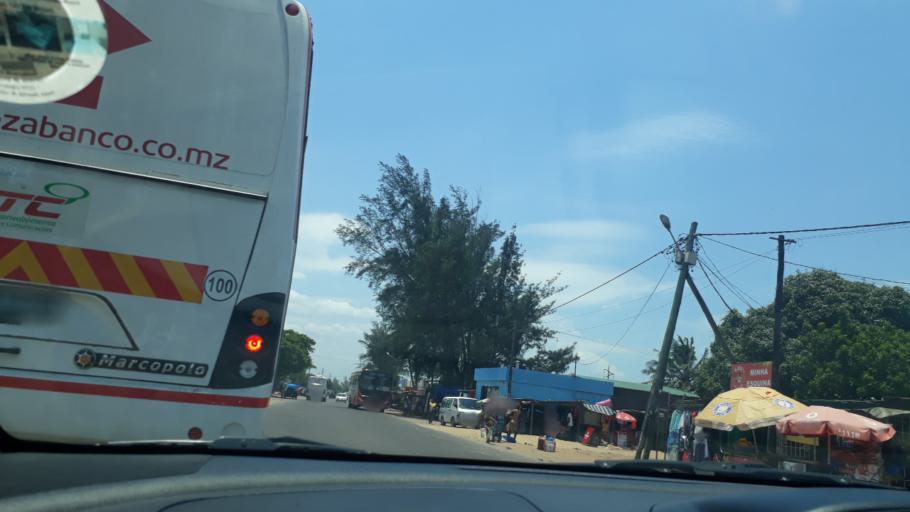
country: MZ
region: Maputo City
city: Maputo
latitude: -25.8977
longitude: 32.6000
